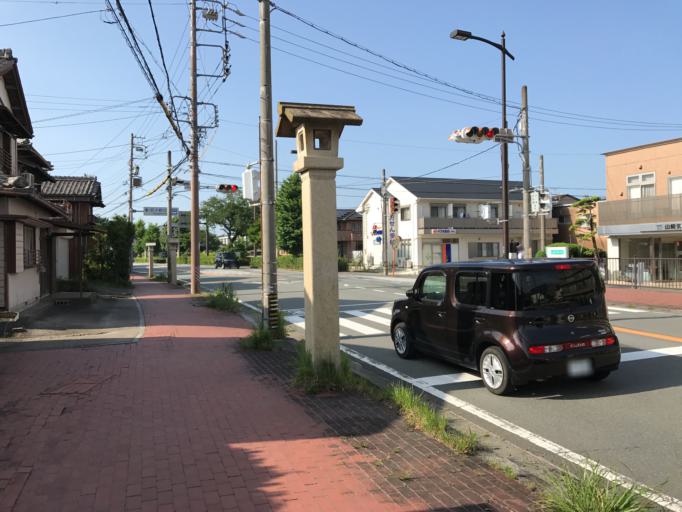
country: JP
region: Mie
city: Ise
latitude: 34.4763
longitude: 136.7290
